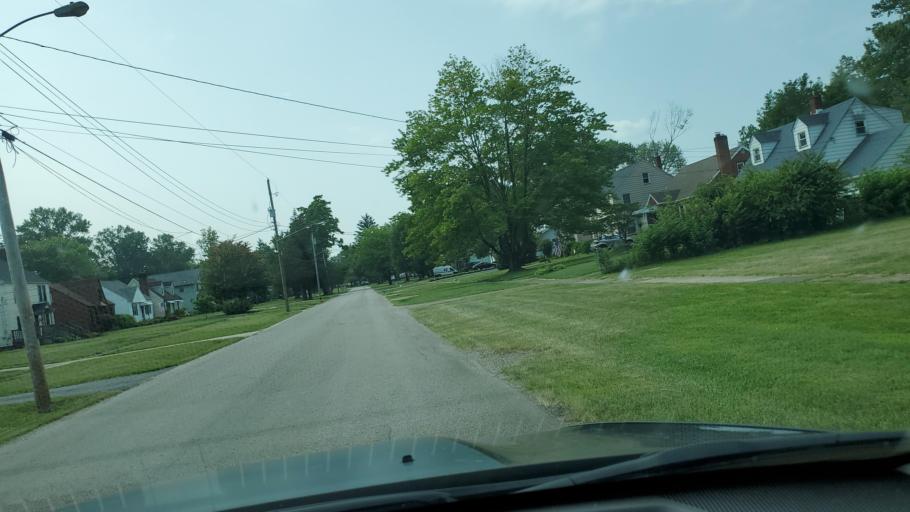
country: US
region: Ohio
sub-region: Trumbull County
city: Bolindale
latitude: 41.2292
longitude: -80.7814
